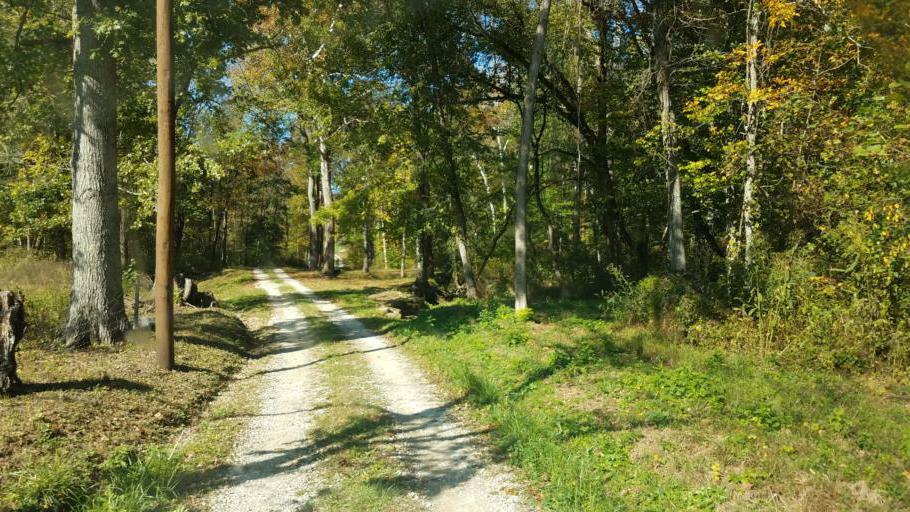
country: US
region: Kentucky
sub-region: Fleming County
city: Flemingsburg
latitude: 38.4597
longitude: -83.5703
